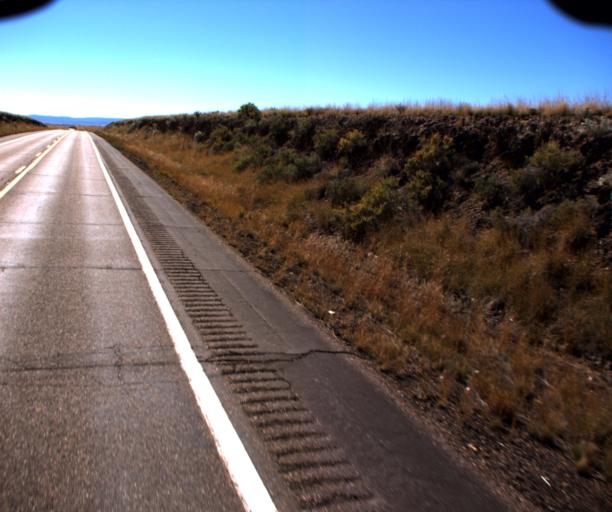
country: US
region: Arizona
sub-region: Apache County
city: Saint Johns
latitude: 34.3132
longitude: -109.3805
